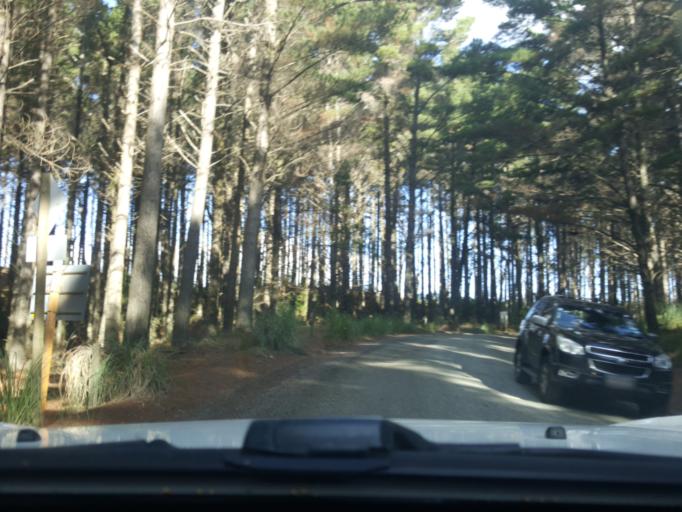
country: NZ
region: Auckland
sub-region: Auckland
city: Muriwai Beach
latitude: -36.7421
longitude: 174.4226
